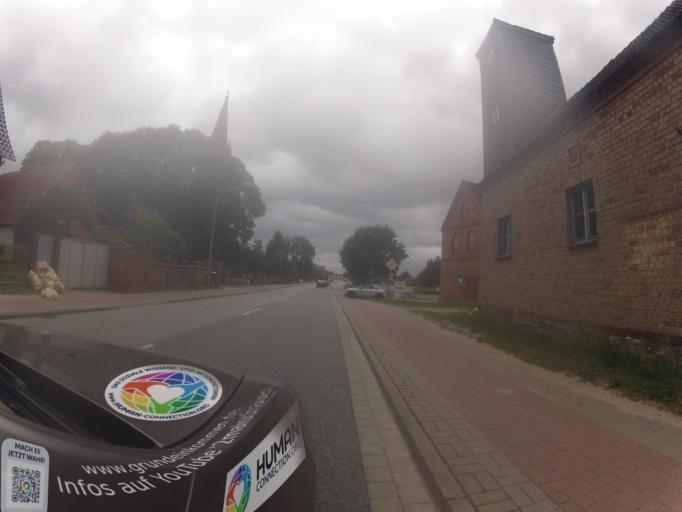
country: DE
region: Mecklenburg-Vorpommern
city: Pasewalk
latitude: 53.5442
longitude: 13.9696
